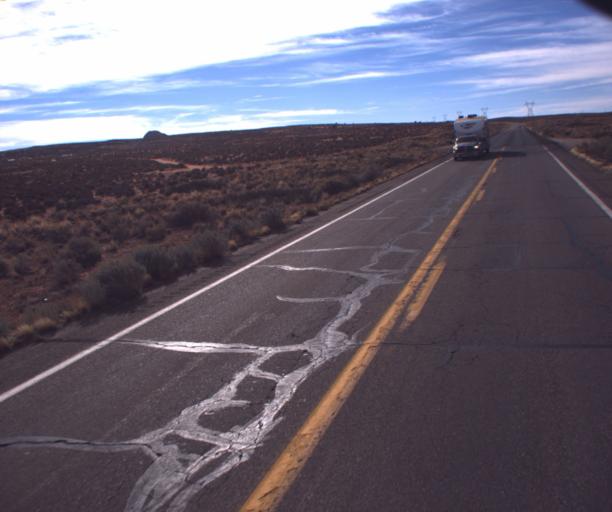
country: US
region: Arizona
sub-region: Coconino County
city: LeChee
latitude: 36.8634
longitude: -111.3393
